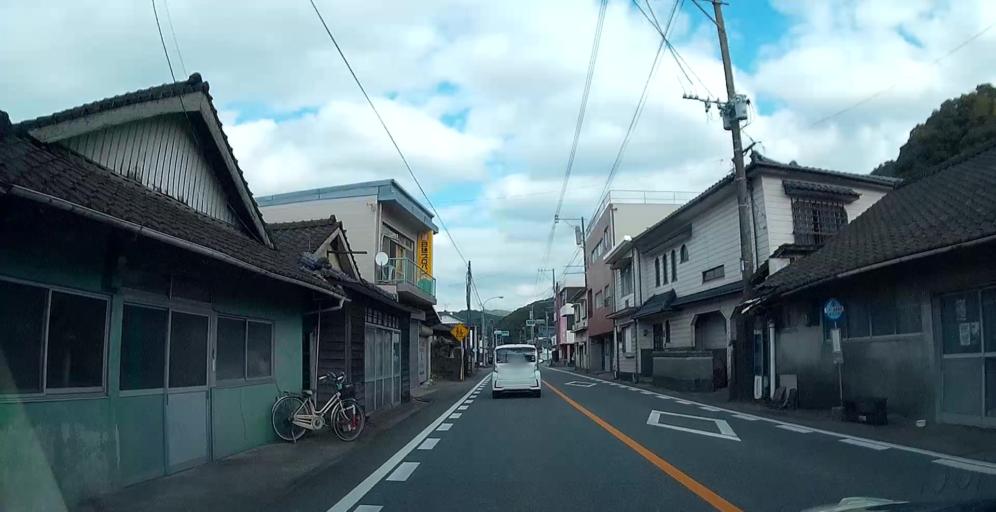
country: JP
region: Kumamoto
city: Yatsushiro
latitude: 32.4366
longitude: 130.5816
